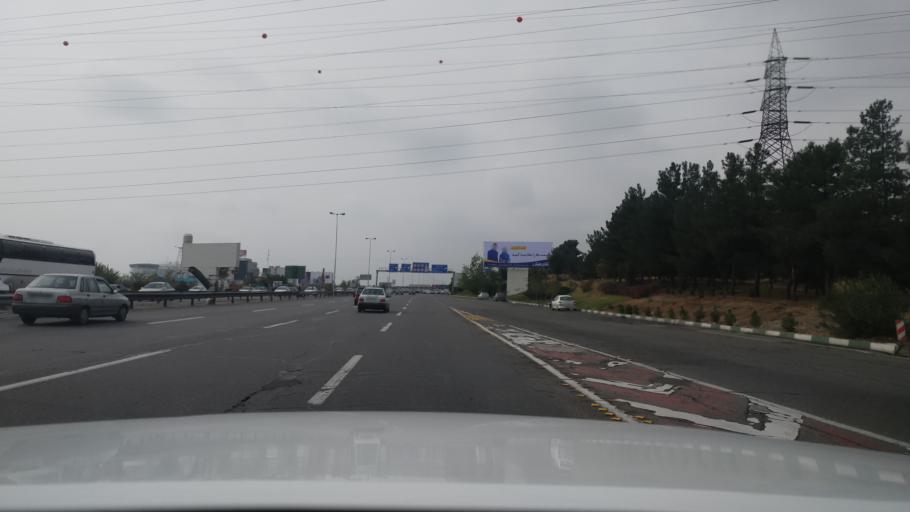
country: IR
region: Tehran
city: Shahr-e Qods
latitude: 35.7150
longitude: 51.2470
